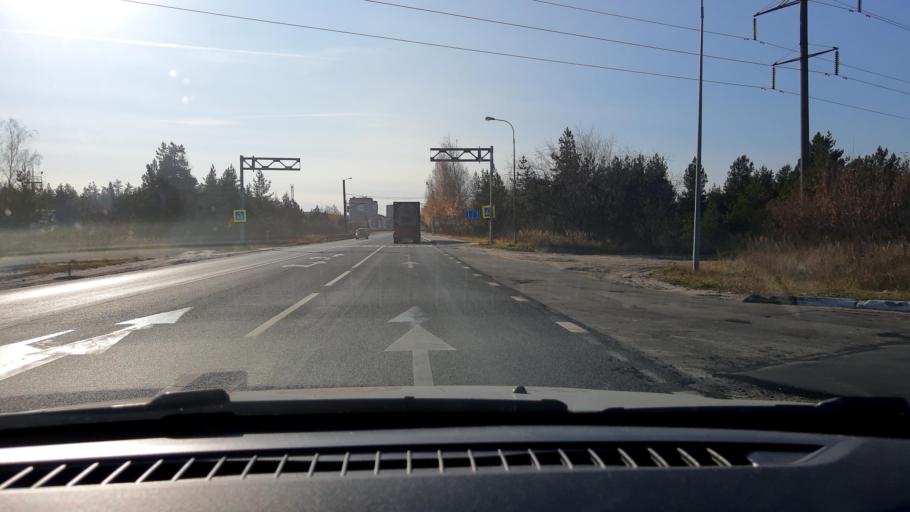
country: RU
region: Nizjnij Novgorod
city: Dzerzhinsk
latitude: 56.2611
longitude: 43.4684
